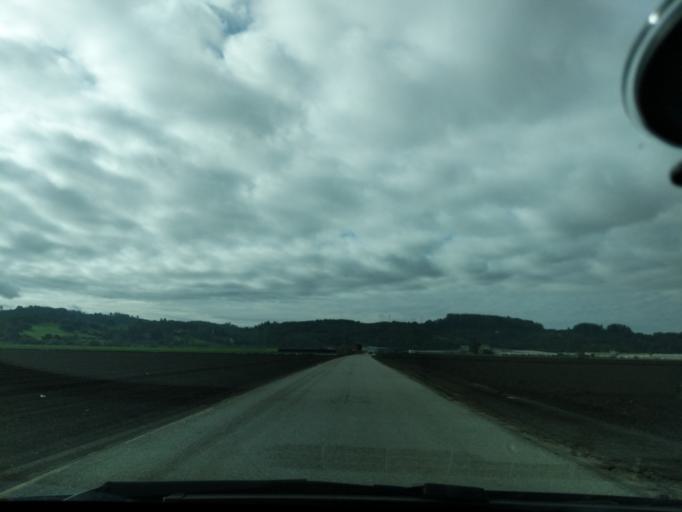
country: US
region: California
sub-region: San Benito County
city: Aromas
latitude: 36.9013
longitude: -121.6703
